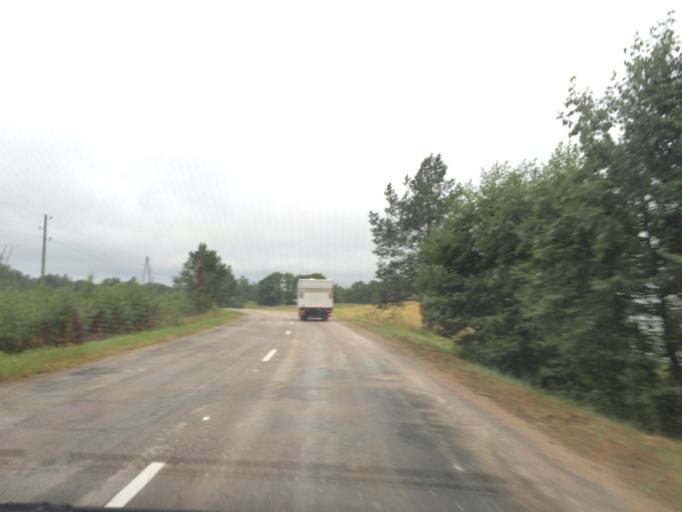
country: LV
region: Ikskile
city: Ikskile
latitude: 56.8557
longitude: 24.5278
